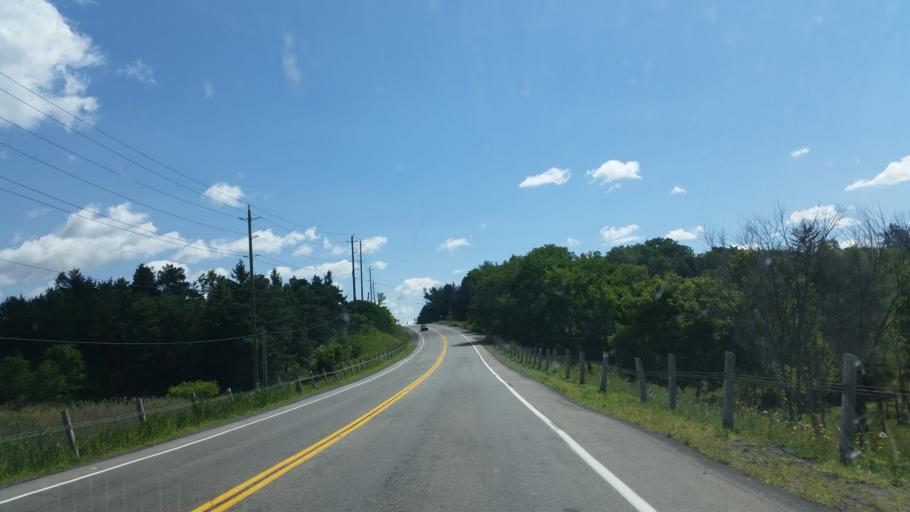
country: CA
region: Ontario
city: Vaughan
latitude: 43.9165
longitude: -79.5826
